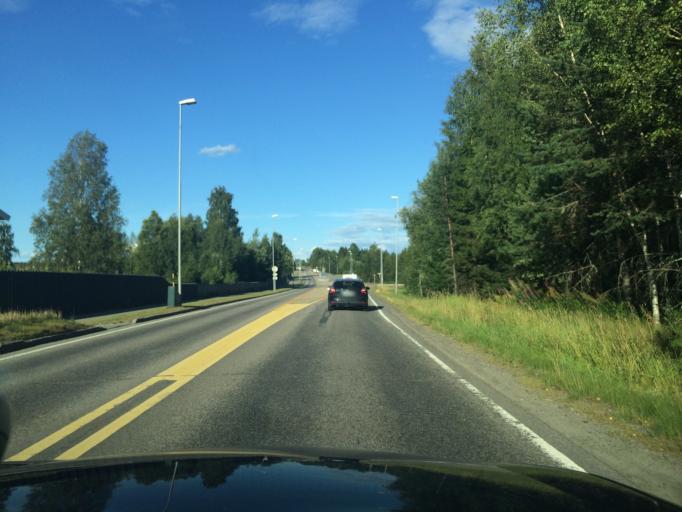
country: NO
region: Hedmark
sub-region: Elverum
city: Elverum
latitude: 60.8940
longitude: 11.5775
